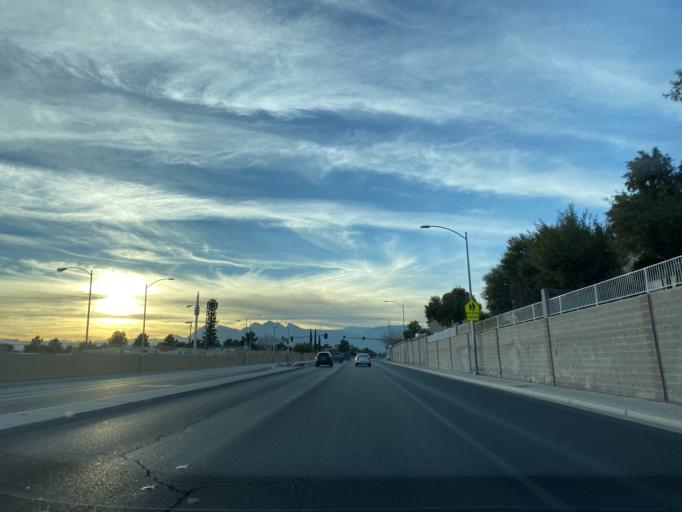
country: US
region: Nevada
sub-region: Clark County
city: North Las Vegas
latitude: 36.2612
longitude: -115.2148
